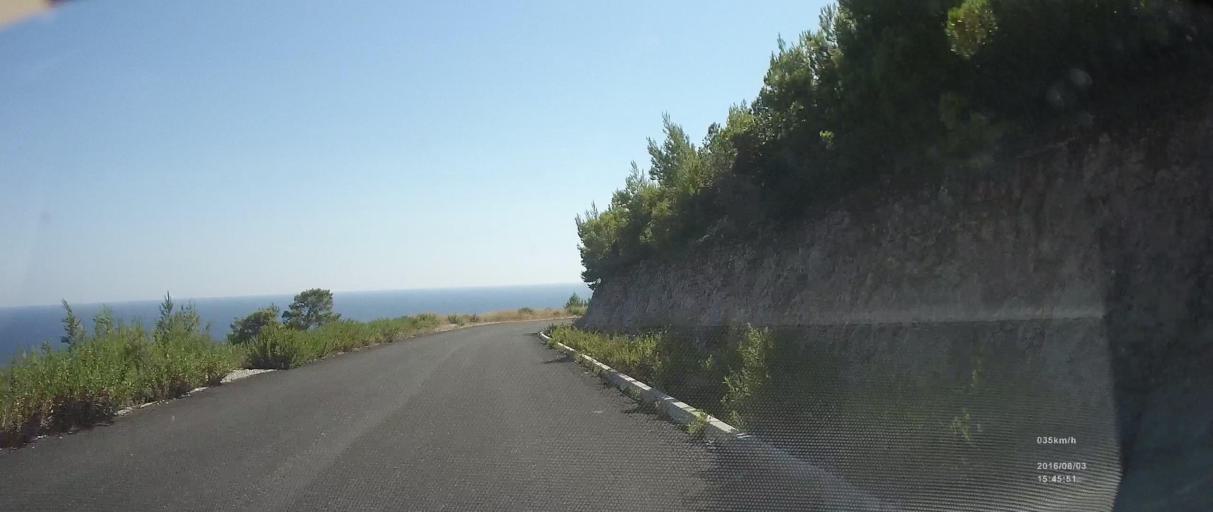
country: HR
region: Dubrovacko-Neretvanska
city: Blato
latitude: 42.7361
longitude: 17.5175
